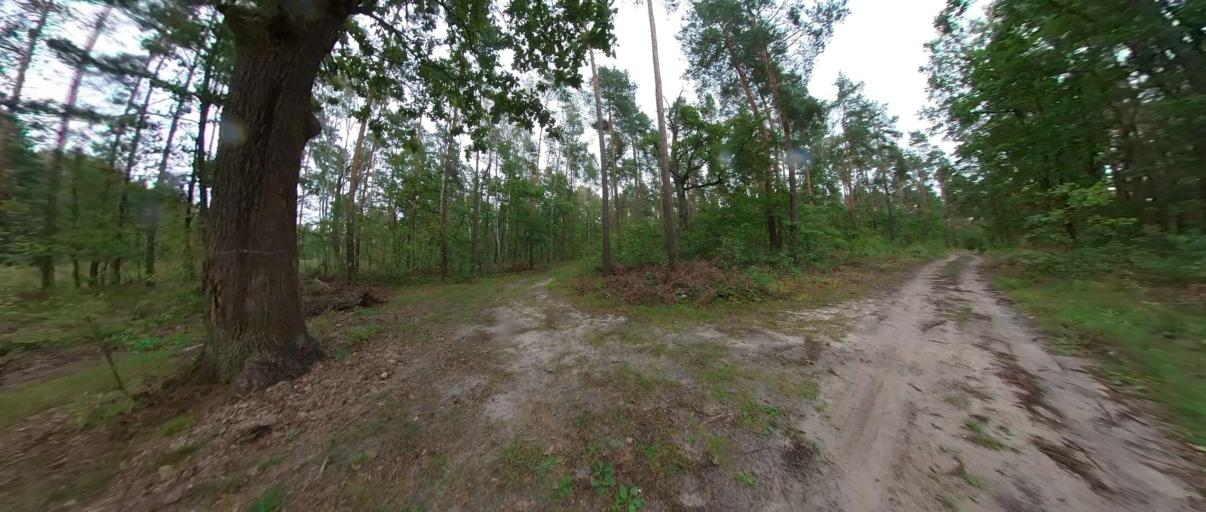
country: PL
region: Masovian Voivodeship
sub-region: Powiat bialobrzeski
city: Bialobrzegi
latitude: 51.6460
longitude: 20.9712
